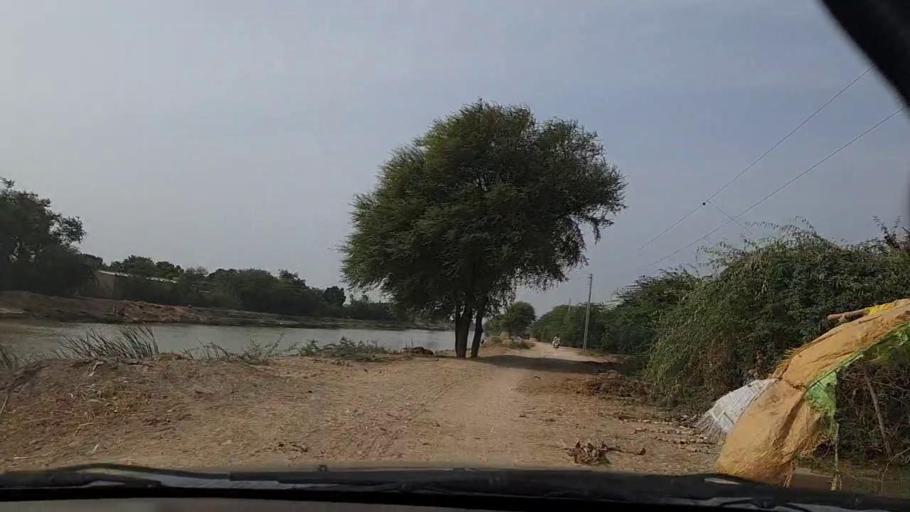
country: PK
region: Sindh
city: Thatta
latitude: 24.5704
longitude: 67.8575
